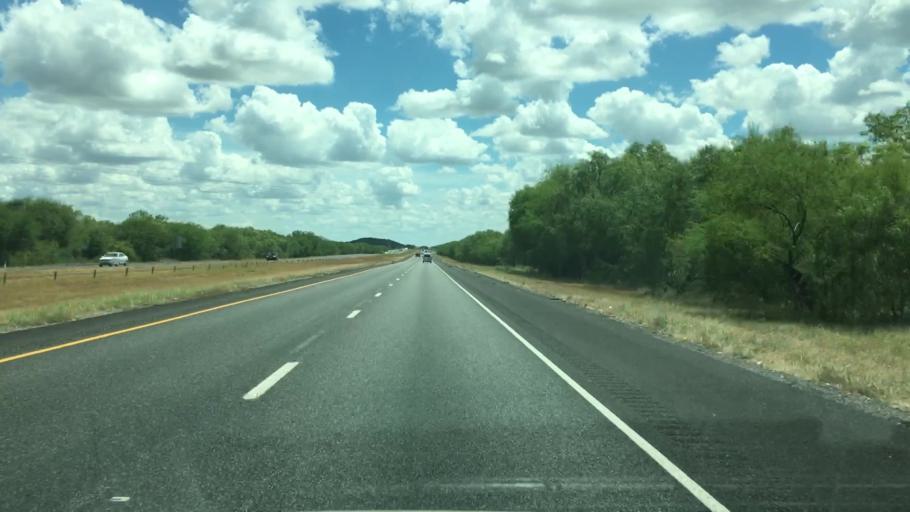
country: US
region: Texas
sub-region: Atascosa County
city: Pleasanton
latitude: 28.7461
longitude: -98.2937
